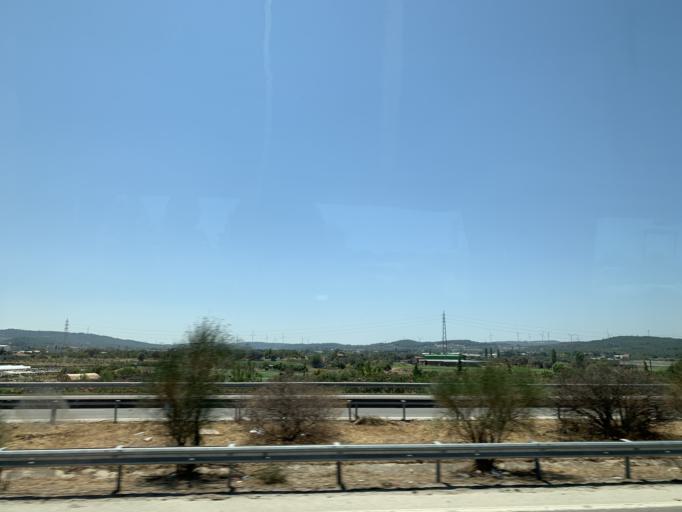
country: TR
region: Izmir
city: Urla
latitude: 38.2967
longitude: 26.7322
